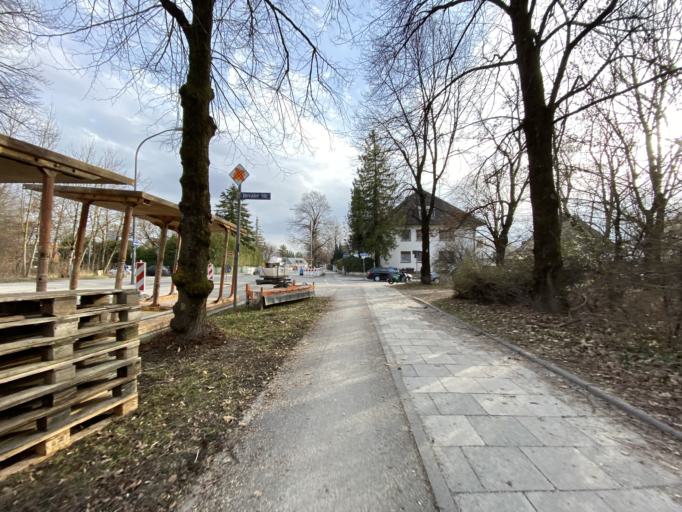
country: DE
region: Bavaria
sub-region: Upper Bavaria
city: Bogenhausen
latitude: 48.1446
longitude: 11.6276
